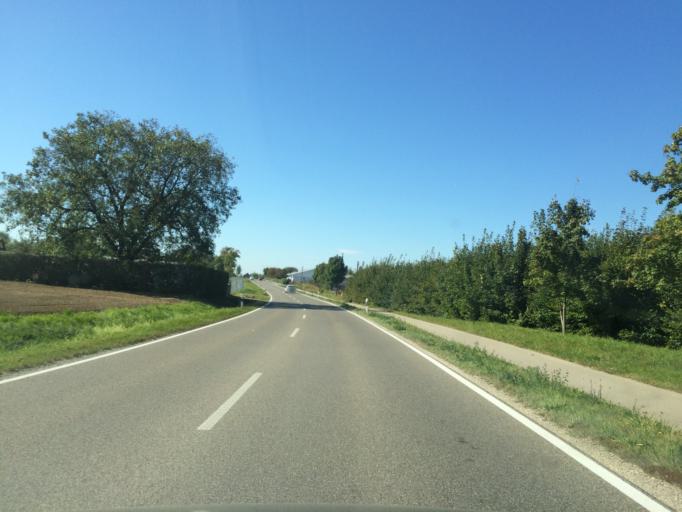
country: DE
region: Bavaria
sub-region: Swabia
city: Friedberg
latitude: 48.3484
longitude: 11.0033
